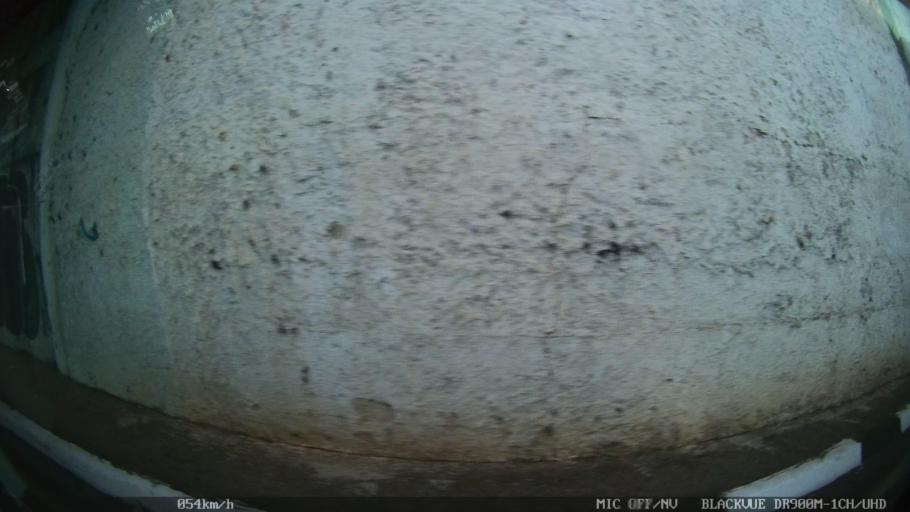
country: BR
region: Sao Paulo
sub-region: Franca
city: Franca
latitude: -20.5333
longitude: -47.4055
